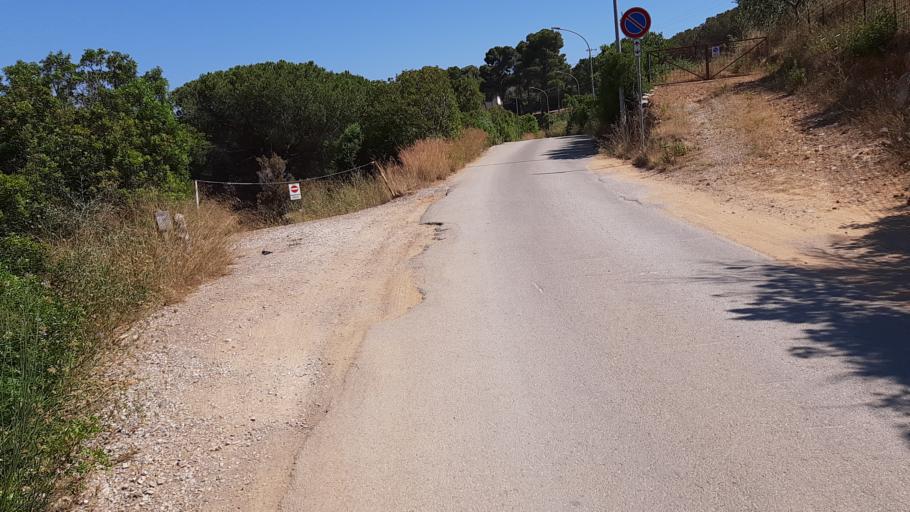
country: IT
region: Tuscany
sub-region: Provincia di Livorno
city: Portoferraio
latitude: 42.7606
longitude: 10.2976
